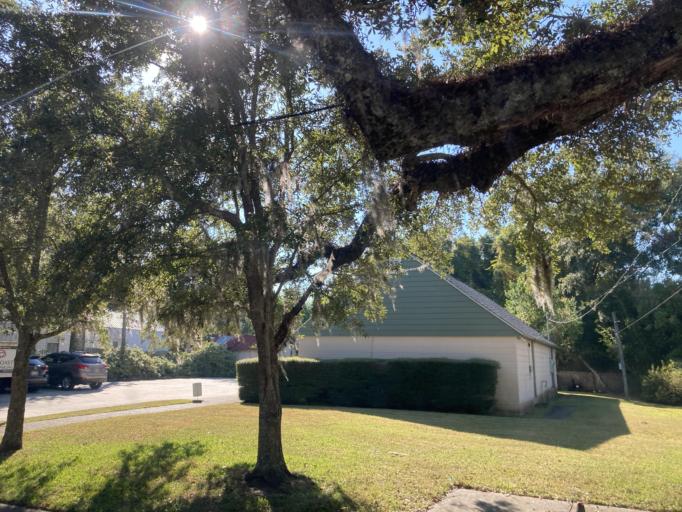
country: US
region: Mississippi
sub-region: Jackson County
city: Ocean Springs
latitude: 30.4103
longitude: -88.8299
